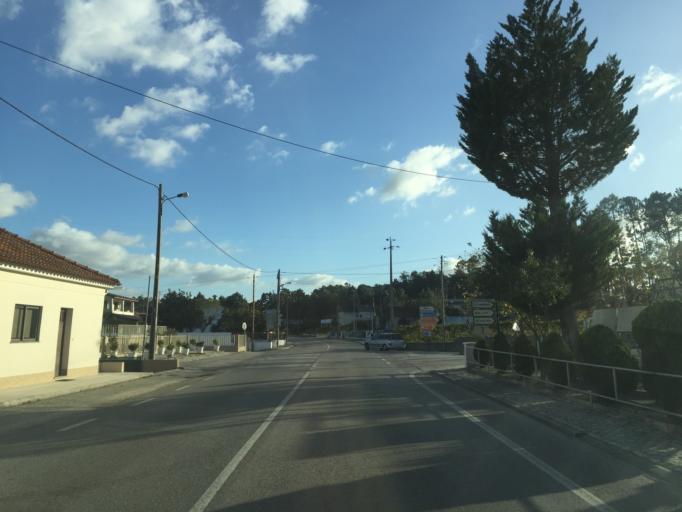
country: PT
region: Leiria
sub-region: Leiria
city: Souto da Carpalhosa
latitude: 39.8279
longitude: -8.8401
